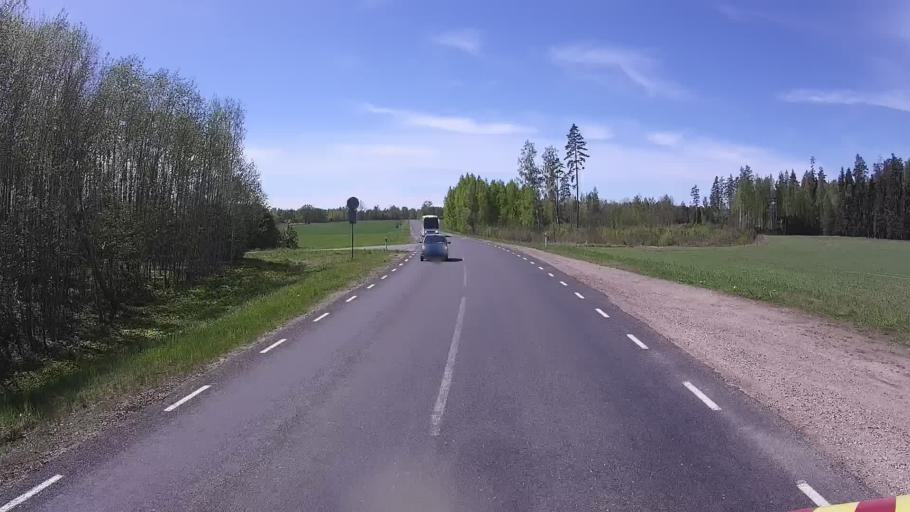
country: EE
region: Polvamaa
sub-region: Raepina vald
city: Rapina
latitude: 58.0195
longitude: 27.3690
